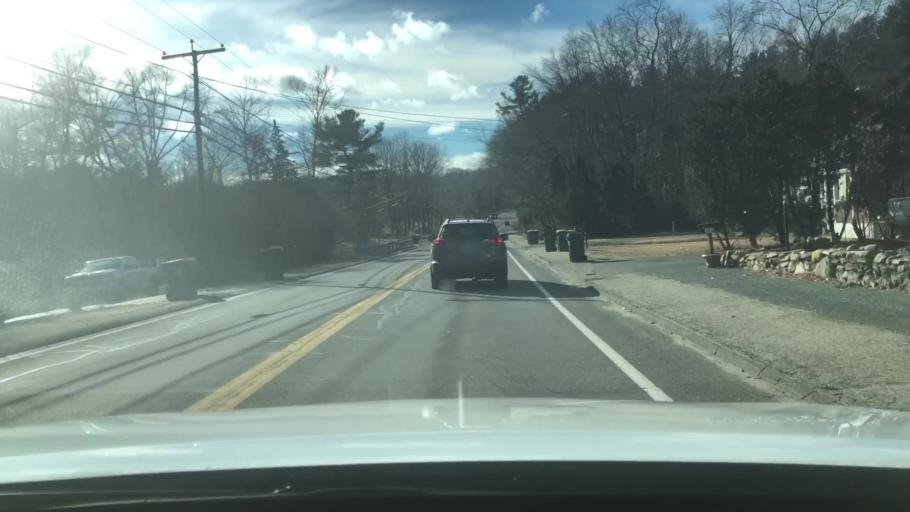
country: US
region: Massachusetts
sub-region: Norfolk County
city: Bellingham
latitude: 42.0682
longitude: -71.4755
